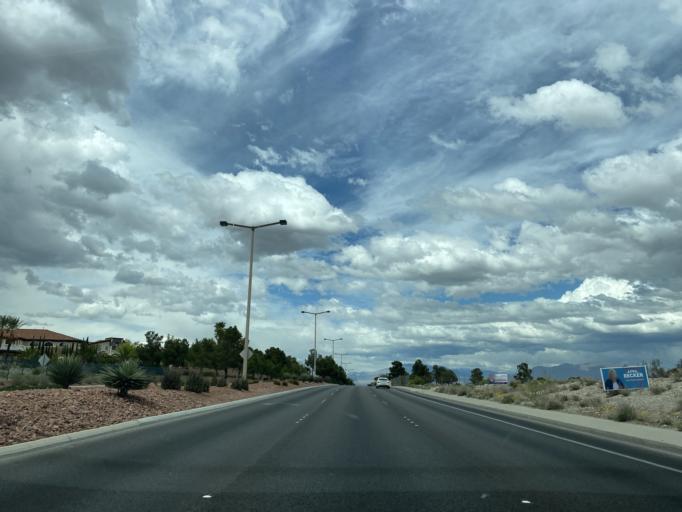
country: US
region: Nevada
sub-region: Clark County
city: Summerlin South
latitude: 36.1804
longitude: -115.2872
